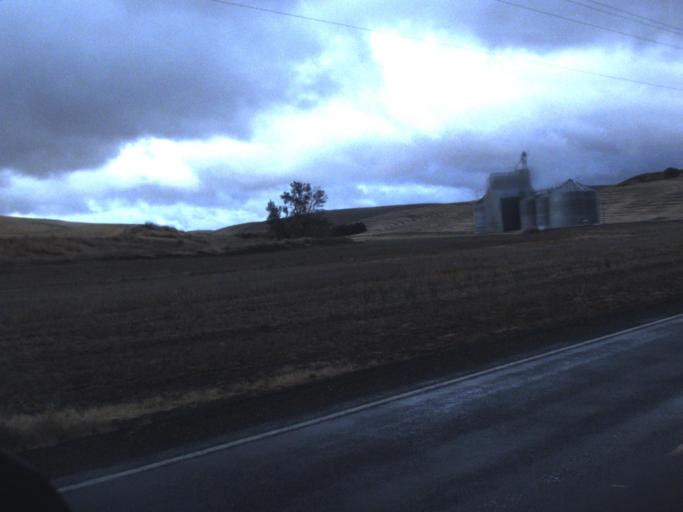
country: US
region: Washington
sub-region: Whitman County
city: Colfax
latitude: 47.0176
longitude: -117.4921
